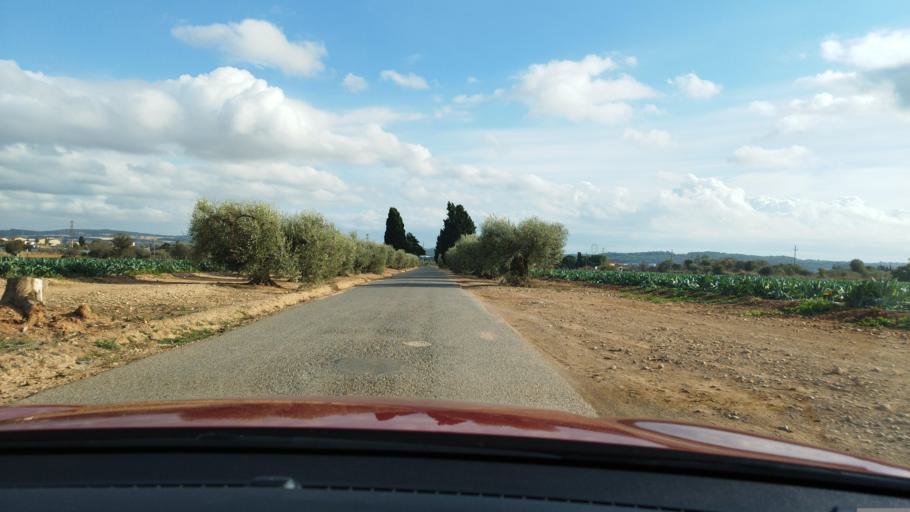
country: ES
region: Catalonia
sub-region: Provincia de Tarragona
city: Santa Oliva
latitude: 41.2522
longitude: 1.5384
